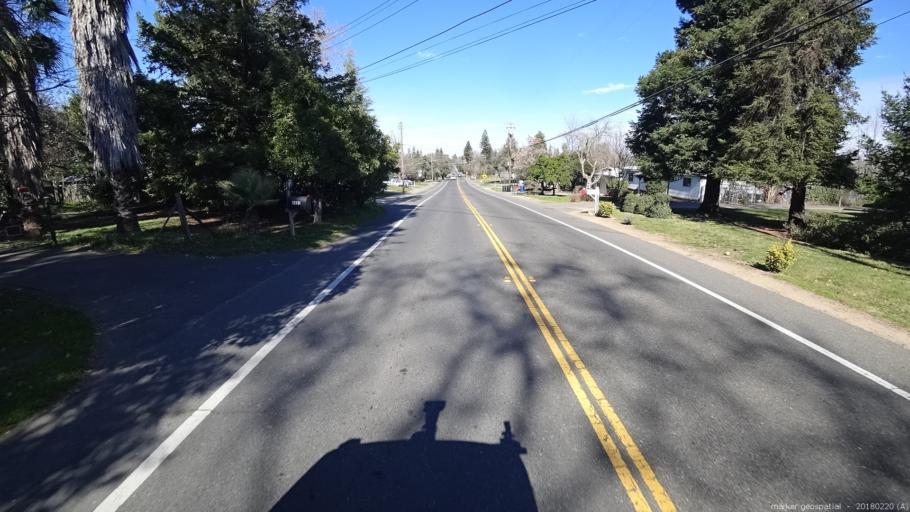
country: US
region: California
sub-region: Sacramento County
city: Orangevale
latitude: 38.6838
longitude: -121.2349
